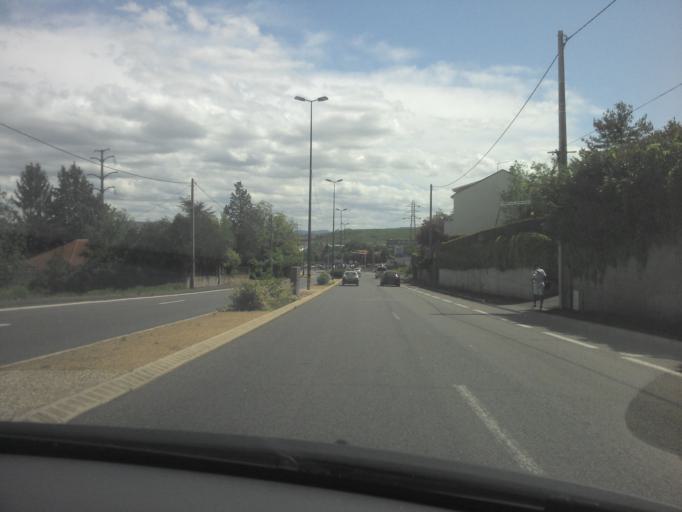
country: FR
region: Auvergne
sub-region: Departement du Puy-de-Dome
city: Aubiere
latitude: 45.7628
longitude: 3.1191
